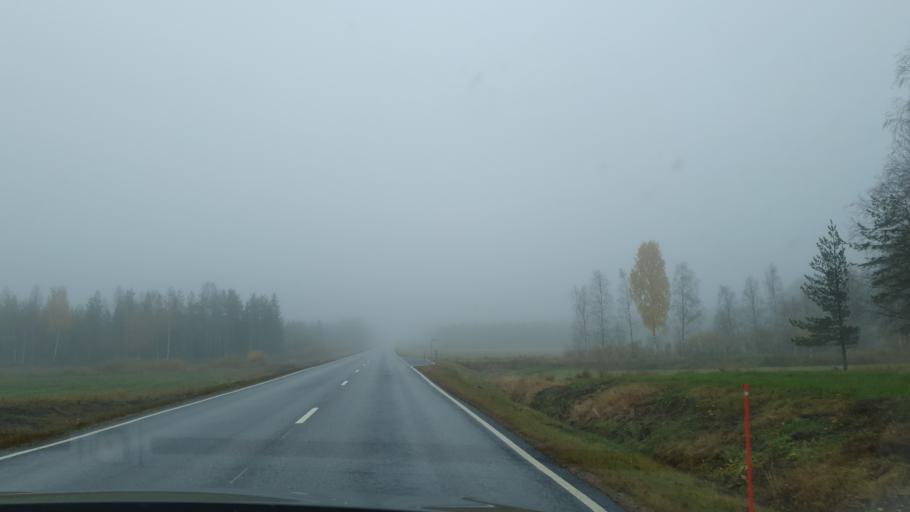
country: FI
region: Lapland
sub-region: Rovaniemi
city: Rovaniemi
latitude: 66.7996
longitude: 25.4142
